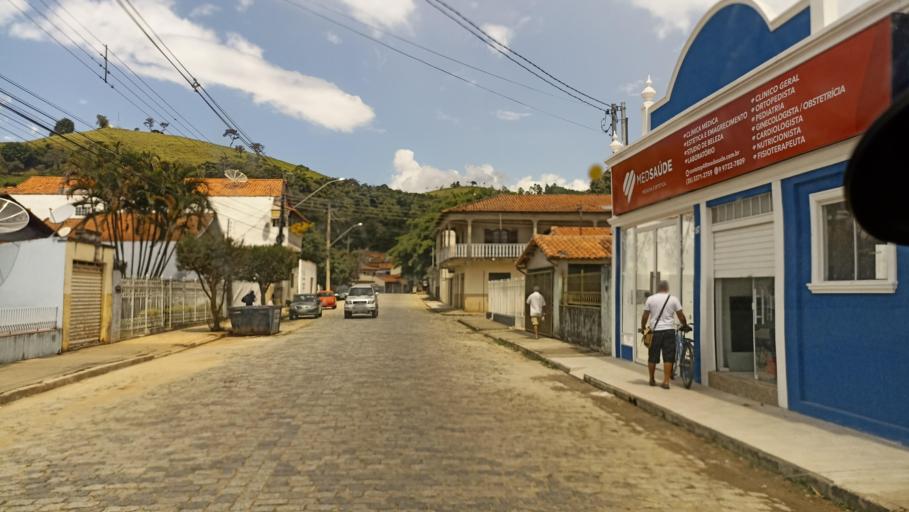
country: BR
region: Minas Gerais
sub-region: Passa Quatro
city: Passa Quatro
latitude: -22.3918
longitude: -44.9646
